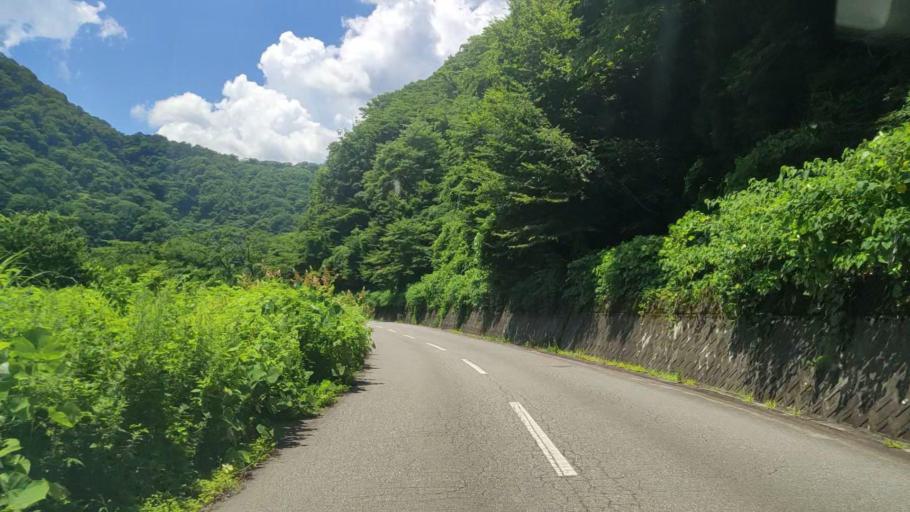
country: JP
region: Fukui
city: Ono
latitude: 35.8965
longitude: 136.5240
